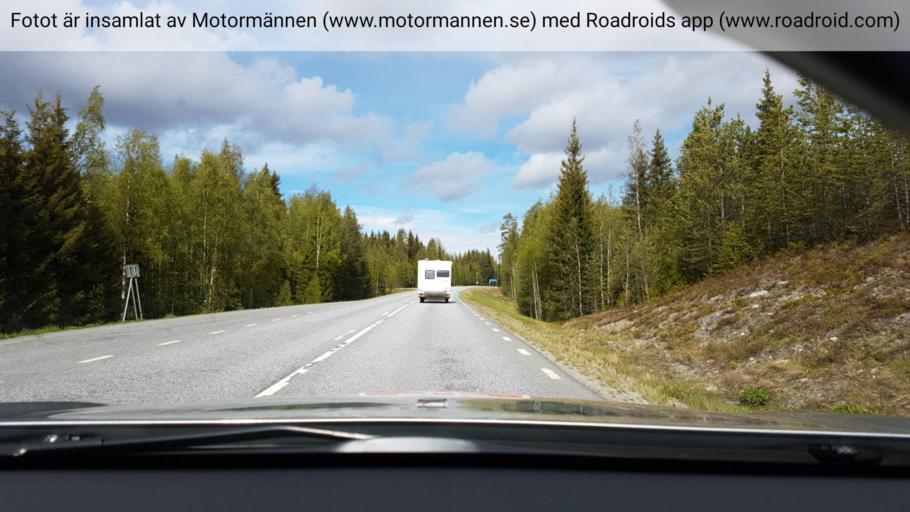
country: SE
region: Vaesterbotten
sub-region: Asele Kommun
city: Asele
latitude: 64.1962
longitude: 17.4937
